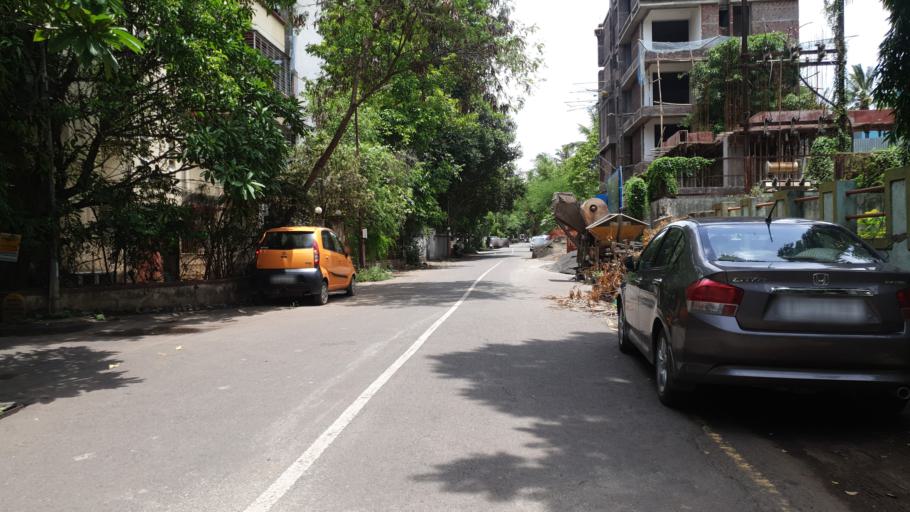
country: IN
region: Maharashtra
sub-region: Pune Division
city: Pune
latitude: 18.4925
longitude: 73.8268
